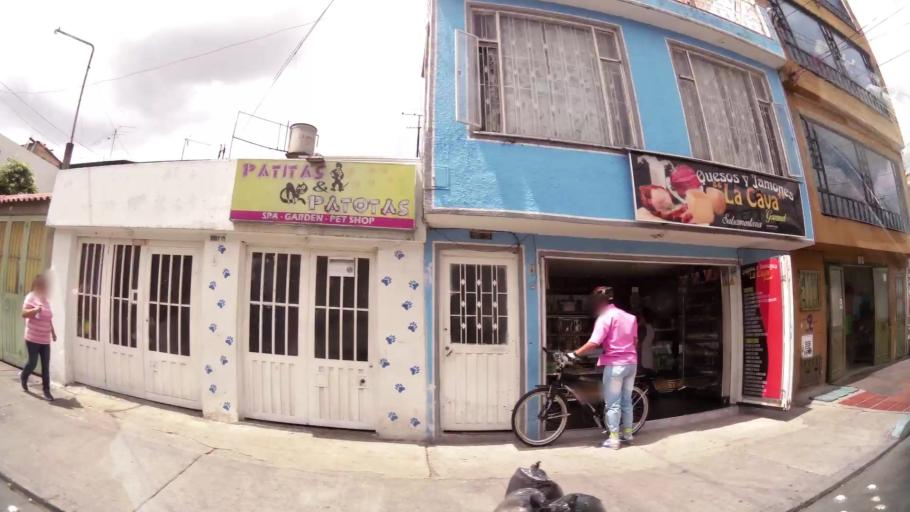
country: CO
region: Cundinamarca
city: Funza
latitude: 4.7065
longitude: -74.1151
